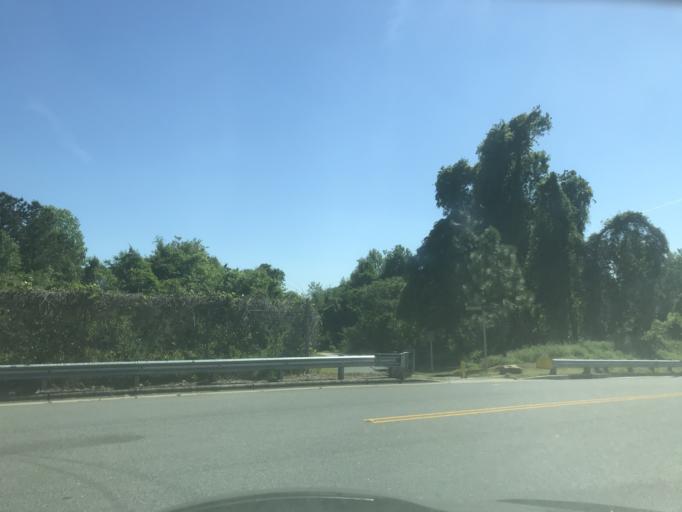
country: US
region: North Carolina
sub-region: Wake County
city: Raleigh
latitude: 35.7584
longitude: -78.6436
